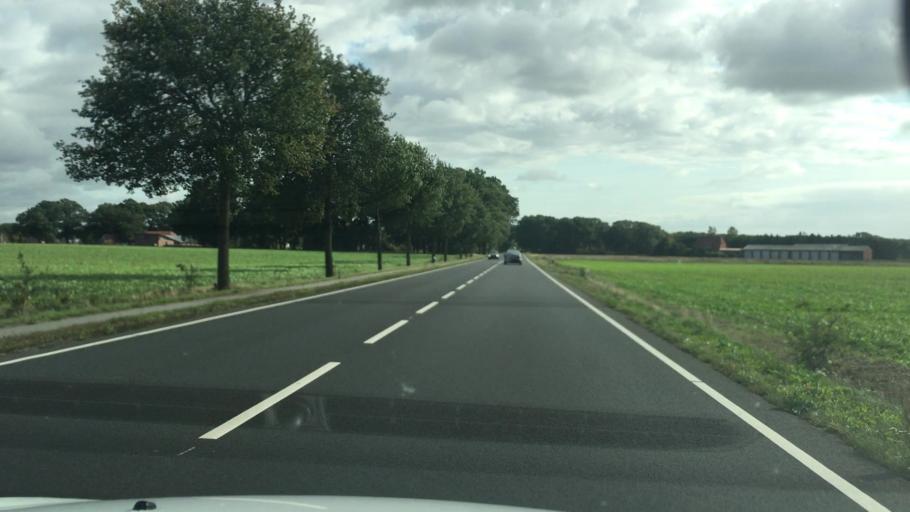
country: DE
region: Lower Saxony
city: Diepholz
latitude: 52.6400
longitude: 8.3487
